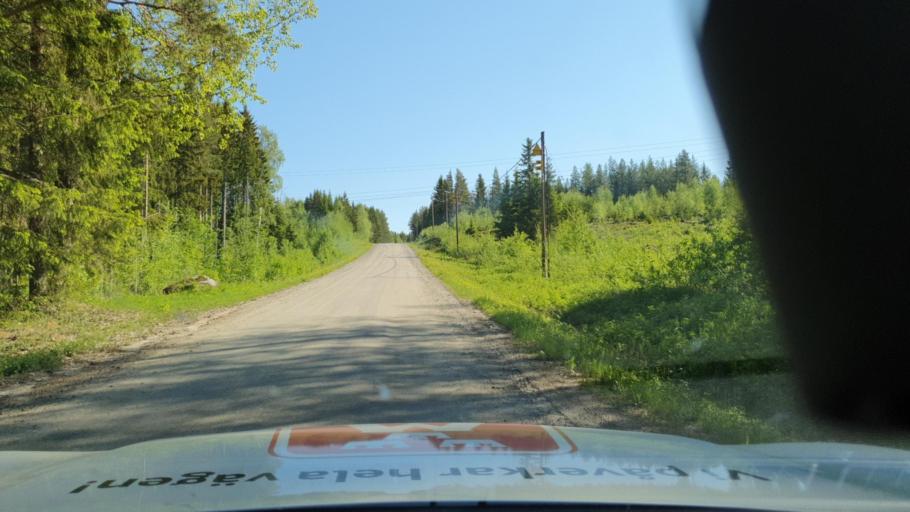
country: SE
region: Vaesterbotten
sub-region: Vannas Kommun
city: Vaennaes
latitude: 63.9840
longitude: 19.7322
